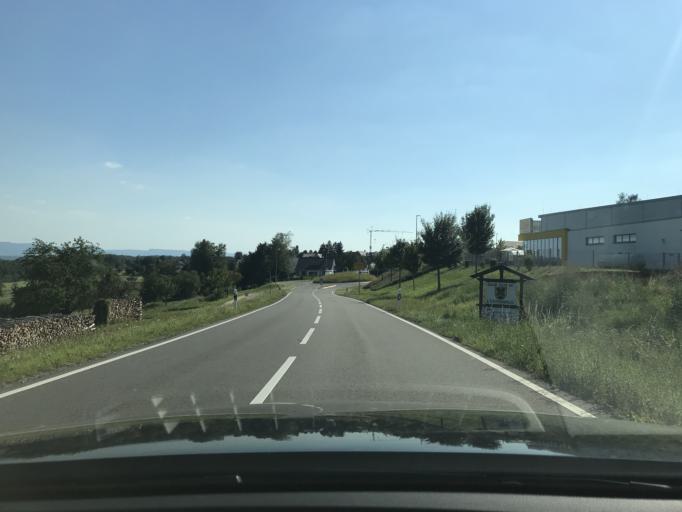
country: DE
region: Baden-Wuerttemberg
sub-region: Regierungsbezirk Stuttgart
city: Baltmannsweiler
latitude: 48.7553
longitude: 9.4869
